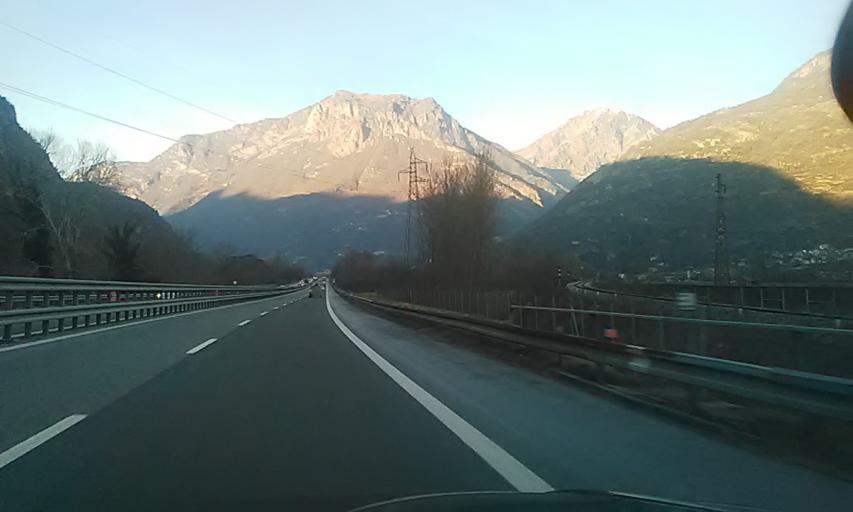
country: IT
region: Piedmont
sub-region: Provincia di Torino
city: Quincinetto
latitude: 45.5720
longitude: 7.8041
